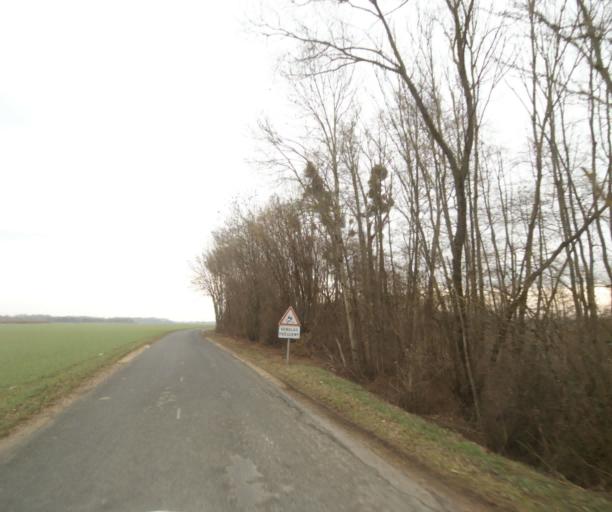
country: FR
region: Champagne-Ardenne
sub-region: Departement de la Haute-Marne
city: Villiers-en-Lieu
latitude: 48.6470
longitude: 4.8337
